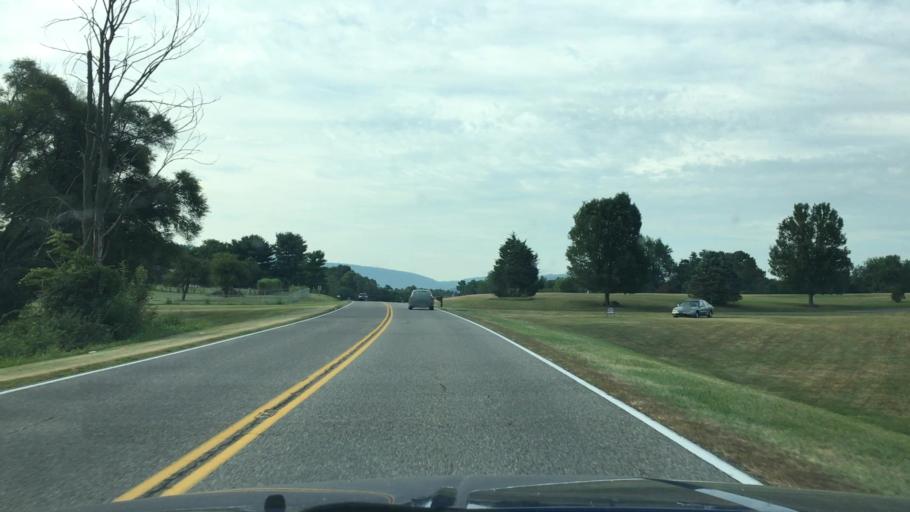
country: US
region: Virginia
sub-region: City of Waynesboro
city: Waynesboro
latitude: 38.1023
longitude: -78.9015
